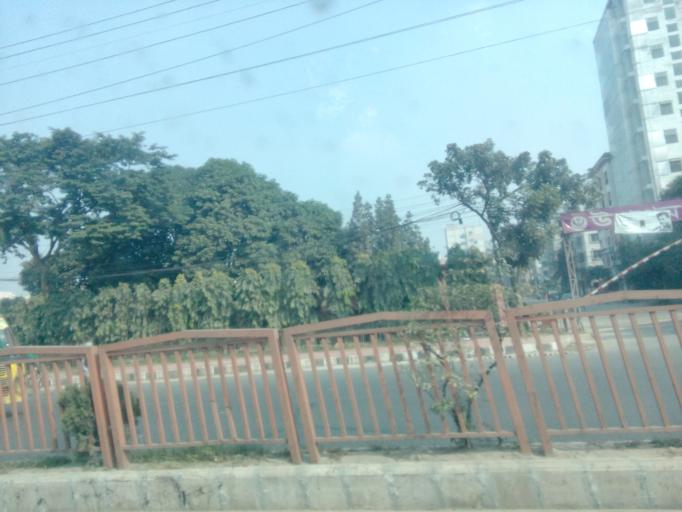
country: BD
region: Dhaka
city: Paltan
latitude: 23.7952
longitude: 90.4242
